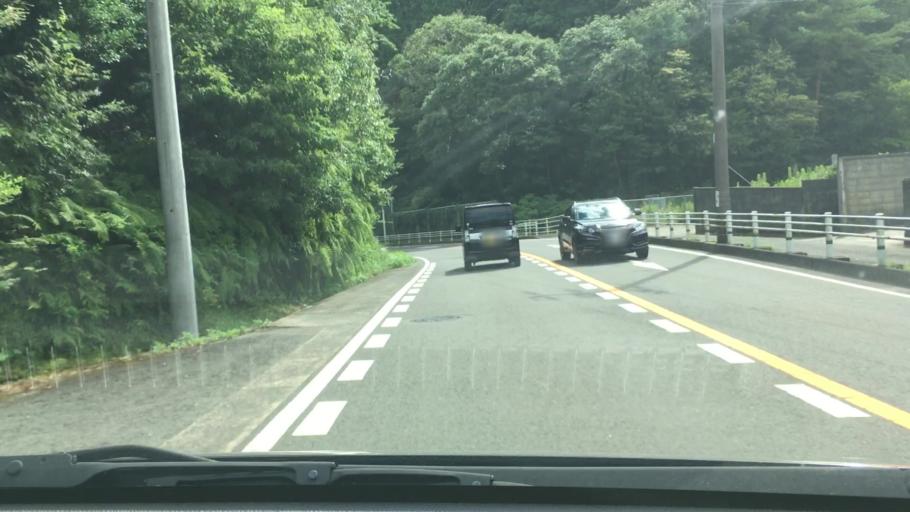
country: JP
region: Nagasaki
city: Togitsu
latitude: 32.9596
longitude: 129.7831
